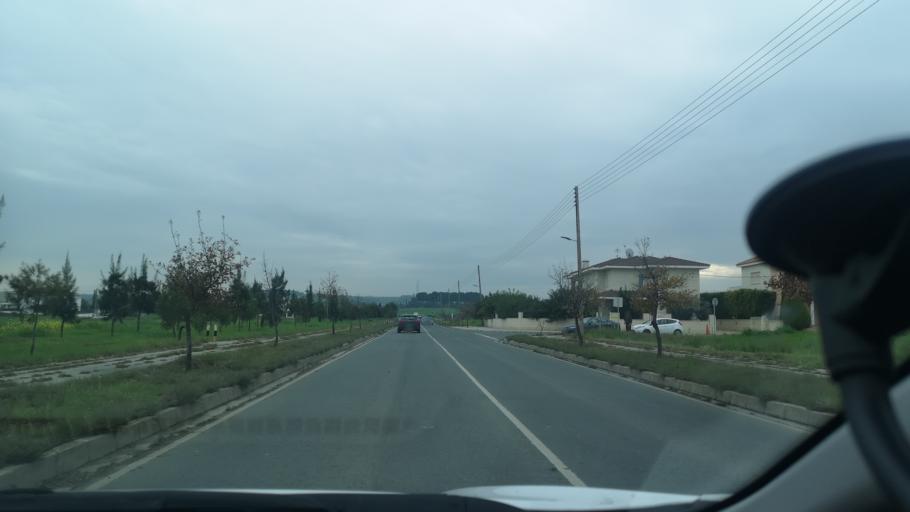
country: CY
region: Lefkosia
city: Tseri
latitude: 35.1048
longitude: 33.3494
